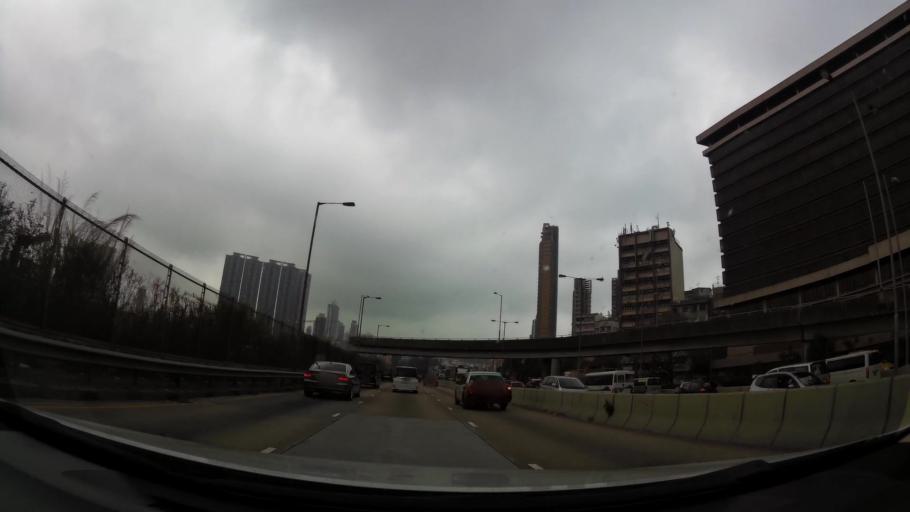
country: HK
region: Kowloon City
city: Kowloon
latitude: 22.3297
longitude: 114.1936
